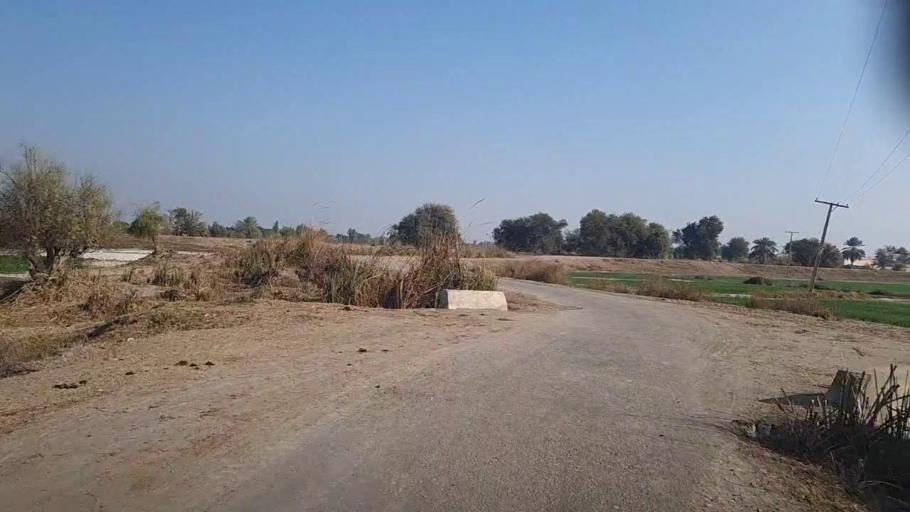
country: PK
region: Sindh
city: Mirpur Mathelo
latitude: 27.8737
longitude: 69.6325
